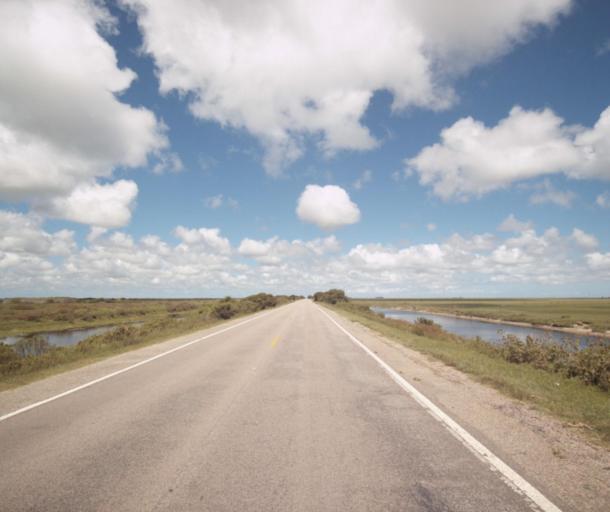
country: BR
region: Rio Grande do Sul
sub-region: Arroio Grande
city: Arroio Grande
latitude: -32.5425
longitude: -52.5409
